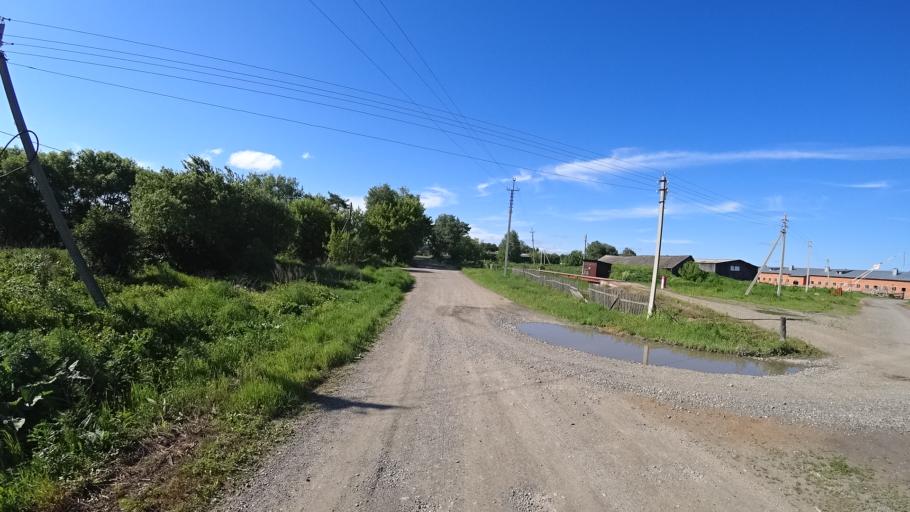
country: RU
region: Khabarovsk Krai
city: Khor
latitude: 47.8874
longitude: 134.9986
